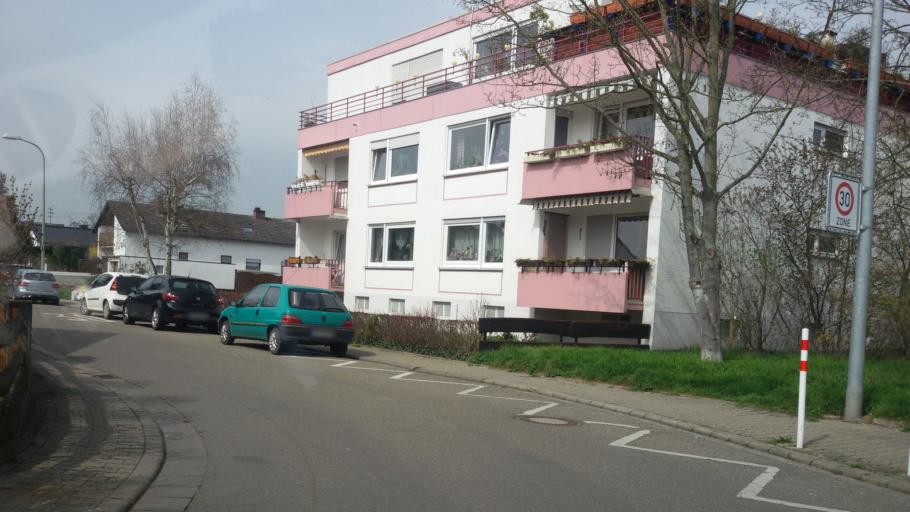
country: DE
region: Rheinland-Pfalz
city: Birkenheide
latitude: 49.4828
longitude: 8.2608
